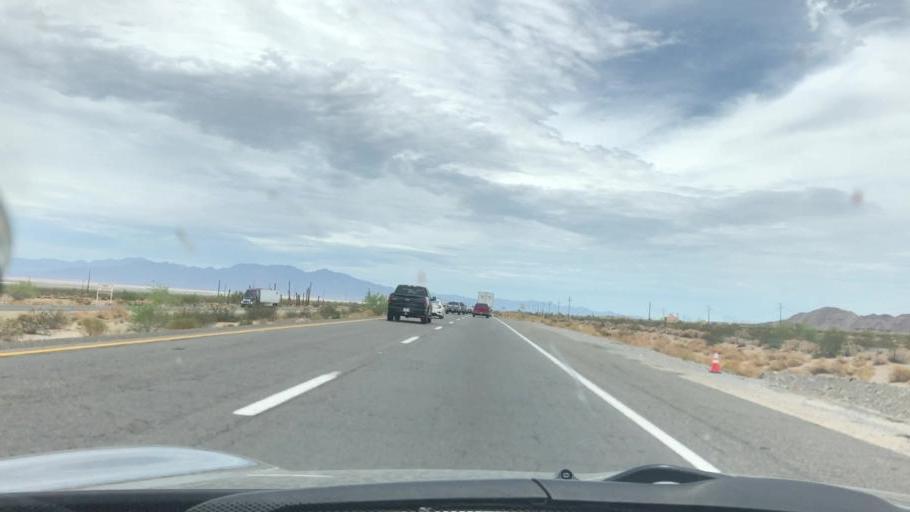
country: US
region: California
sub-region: Imperial County
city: Niland
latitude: 33.7104
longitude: -115.3925
